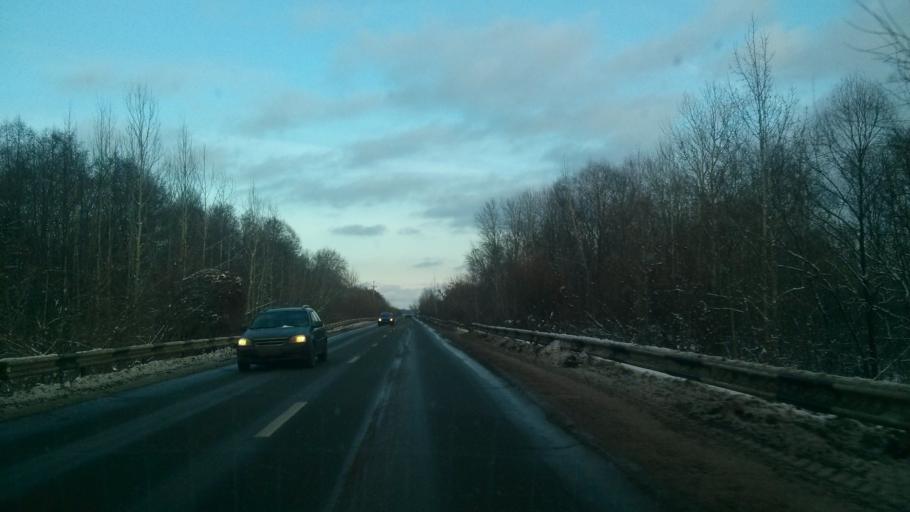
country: RU
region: Nizjnij Novgorod
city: Navashino
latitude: 55.6146
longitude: 42.2188
